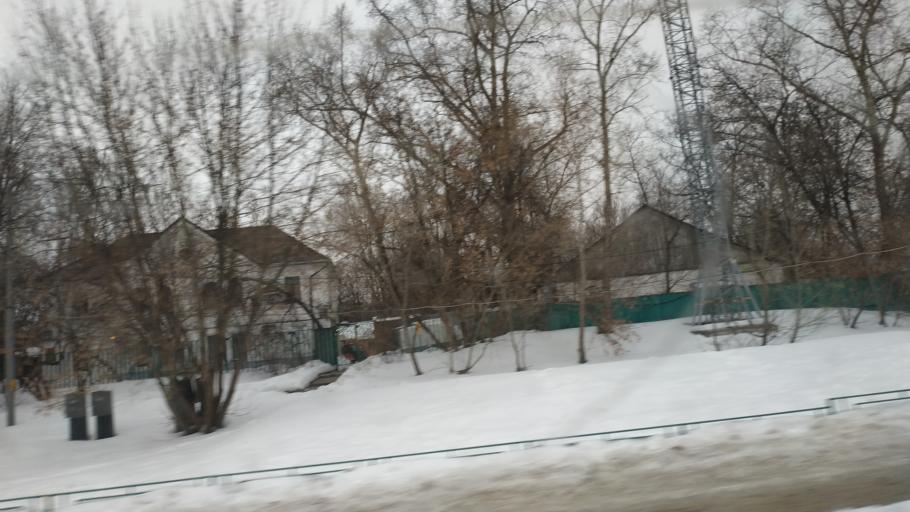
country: RU
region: Moscow
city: Shchukino
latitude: 55.7807
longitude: 37.4401
